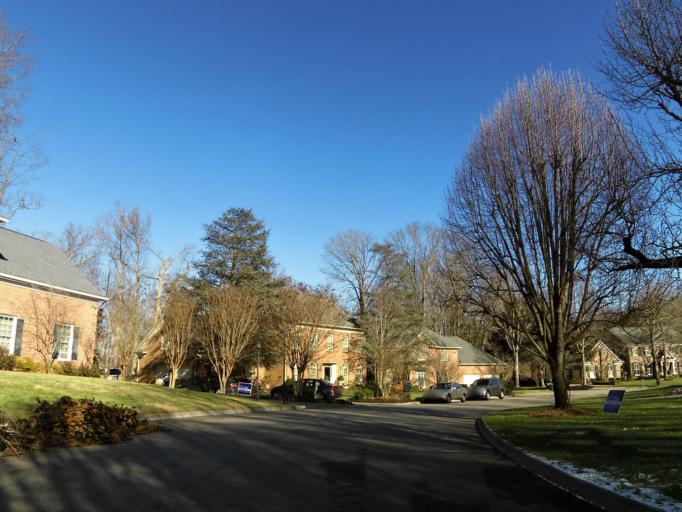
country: US
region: Tennessee
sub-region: Knox County
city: Knoxville
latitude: 35.9238
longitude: -84.0134
